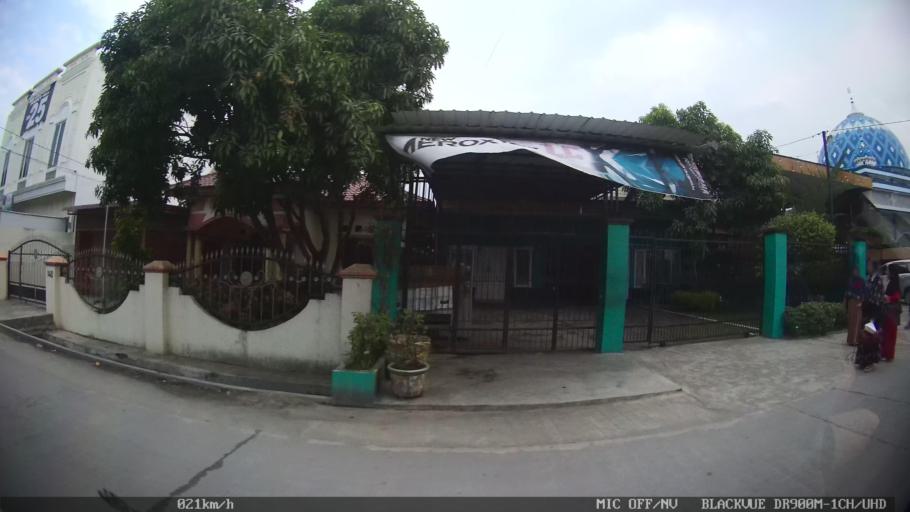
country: ID
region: North Sumatra
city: Medan
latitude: 3.6093
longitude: 98.7031
